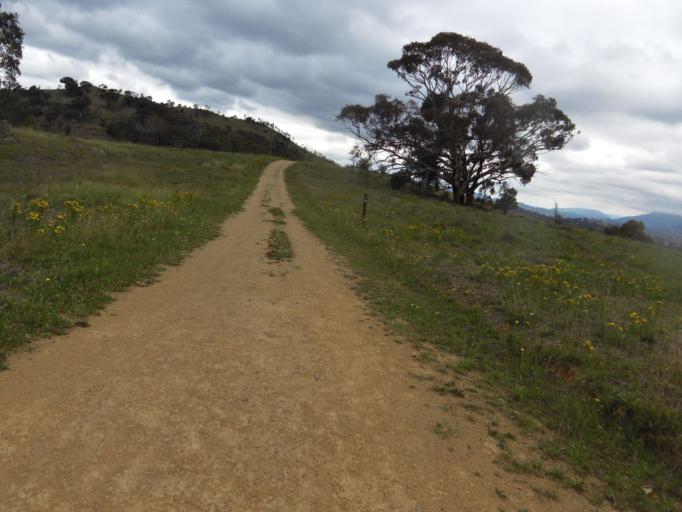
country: AU
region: Australian Capital Territory
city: Macarthur
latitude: -35.3645
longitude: 149.0401
